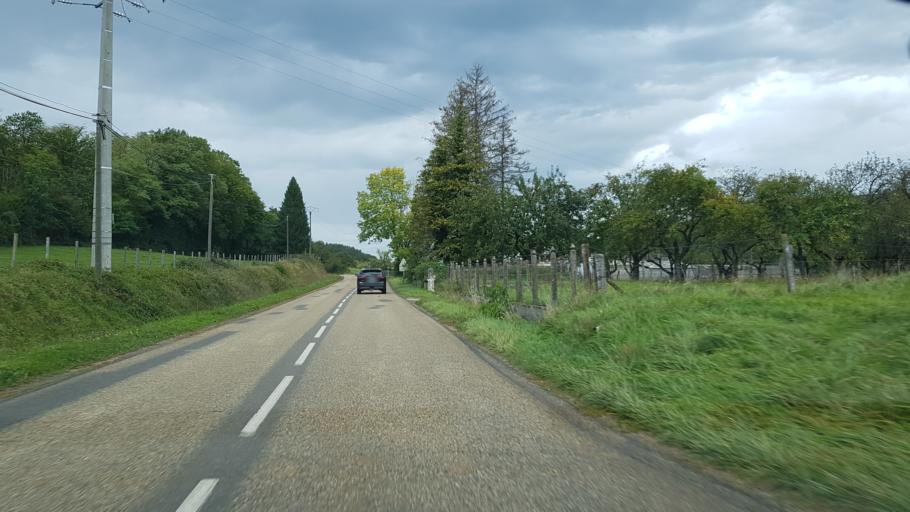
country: FR
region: Rhone-Alpes
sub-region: Departement de l'Ain
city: Cuisiat
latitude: 46.3044
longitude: 5.4399
